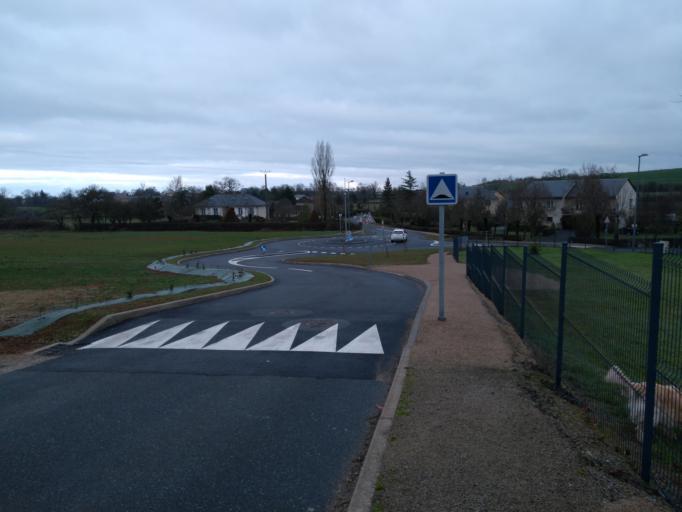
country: FR
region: Midi-Pyrenees
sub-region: Departement de l'Aveyron
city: Sainte-Radegonde
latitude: 44.3427
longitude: 2.6245
